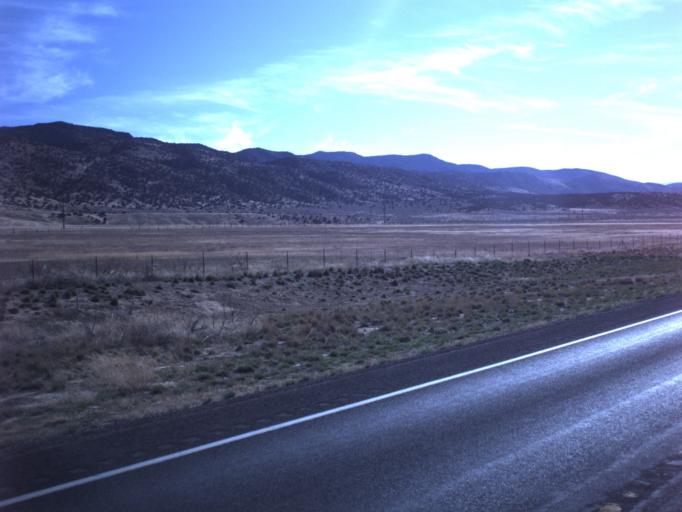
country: US
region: Utah
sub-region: Sanpete County
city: Gunnison
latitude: 39.3103
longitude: -111.9000
